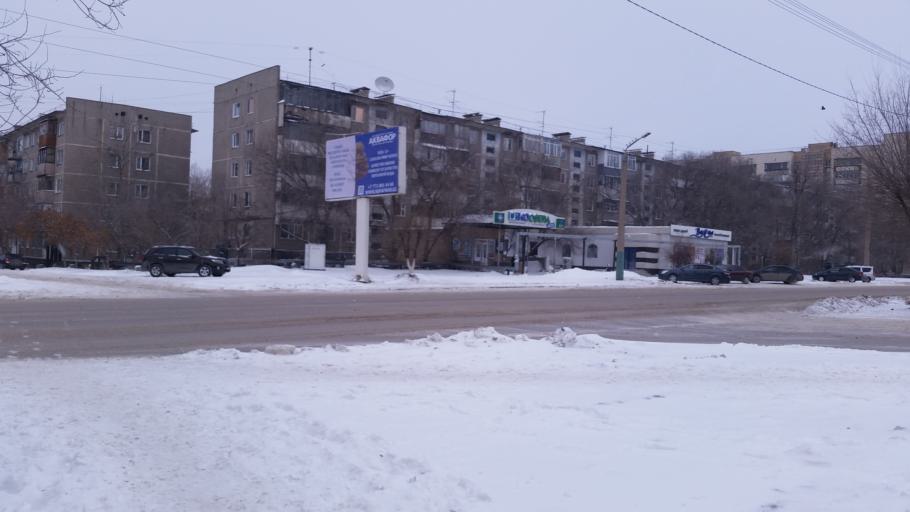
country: KZ
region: Qaraghandy
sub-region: Qaraghandy Qalasy
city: Karagandy
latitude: 49.7752
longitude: 73.1506
